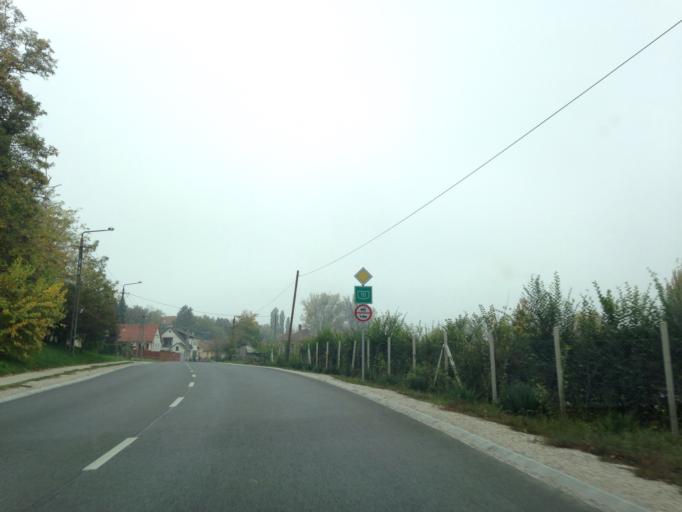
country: HU
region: Komarom-Esztergom
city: Dunaalmas
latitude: 47.7328
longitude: 18.3270
